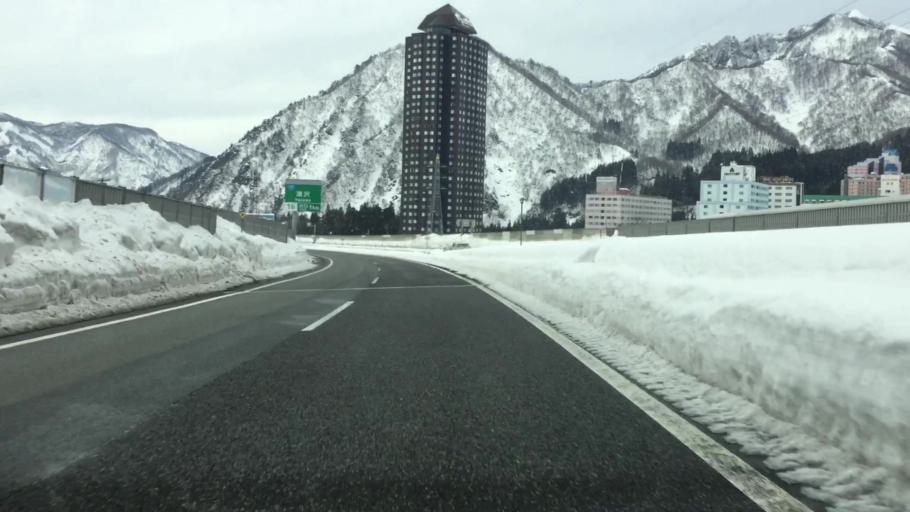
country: JP
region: Niigata
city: Shiozawa
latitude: 36.9272
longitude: 138.8401
